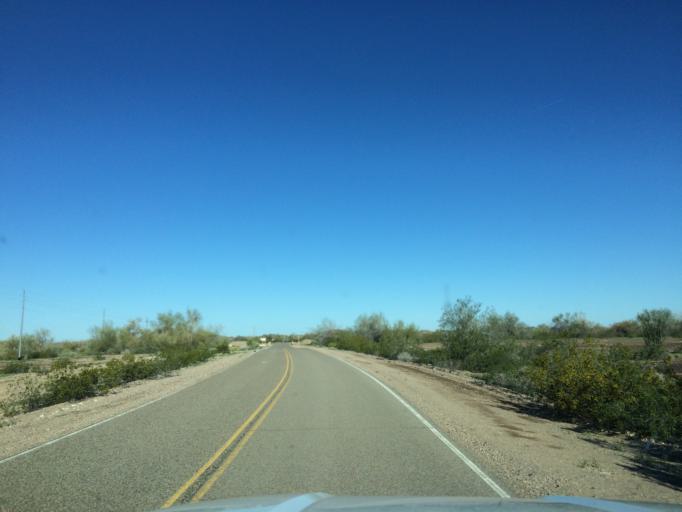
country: US
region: Arizona
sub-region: Yuma County
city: Wellton
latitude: 32.9808
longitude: -114.2697
